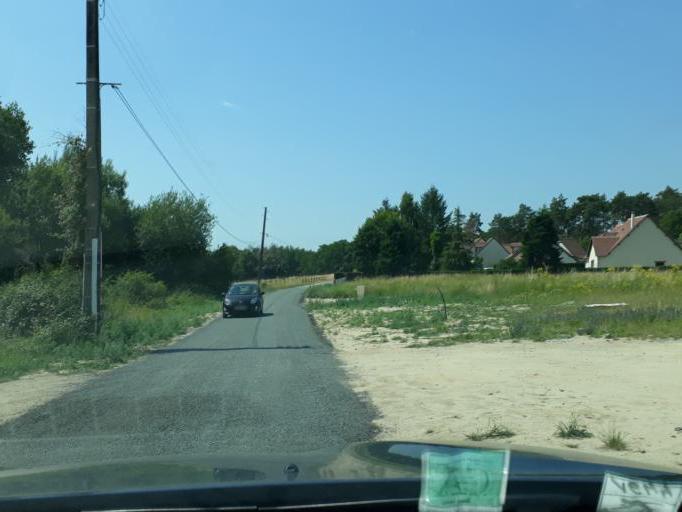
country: FR
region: Centre
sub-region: Departement du Loir-et-Cher
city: Vouzon
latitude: 47.6408
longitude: 2.0538
